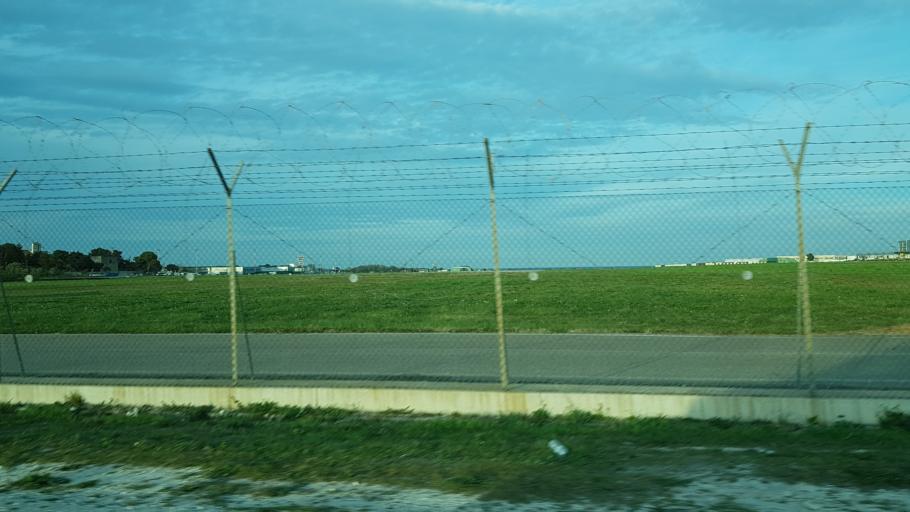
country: IT
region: Apulia
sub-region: Provincia di Brindisi
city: Brindisi
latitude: 40.6504
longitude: 17.9342
